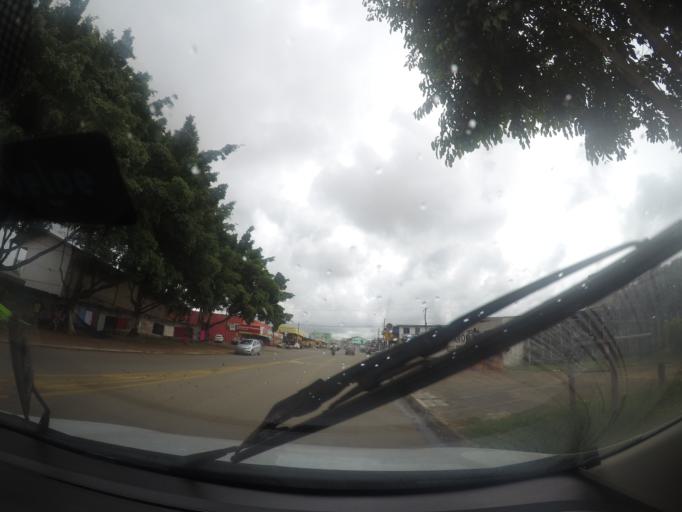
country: BR
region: Goias
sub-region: Trindade
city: Trindade
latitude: -16.6445
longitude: -49.3913
